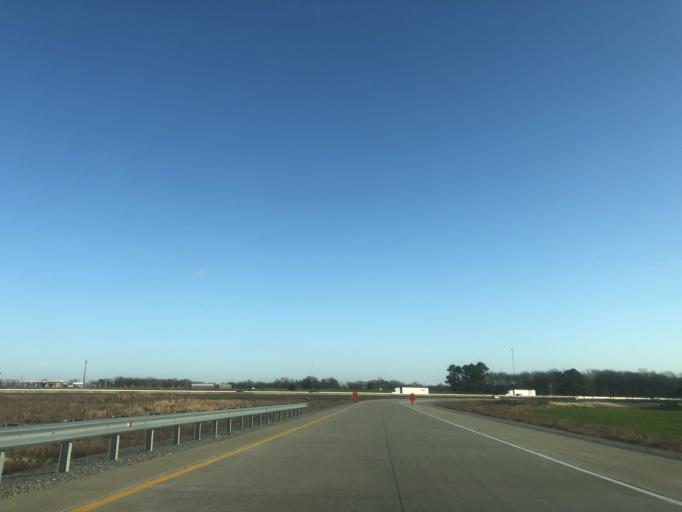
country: US
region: Tennessee
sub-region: Sumner County
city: Portland
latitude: 36.6293
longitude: -86.5773
